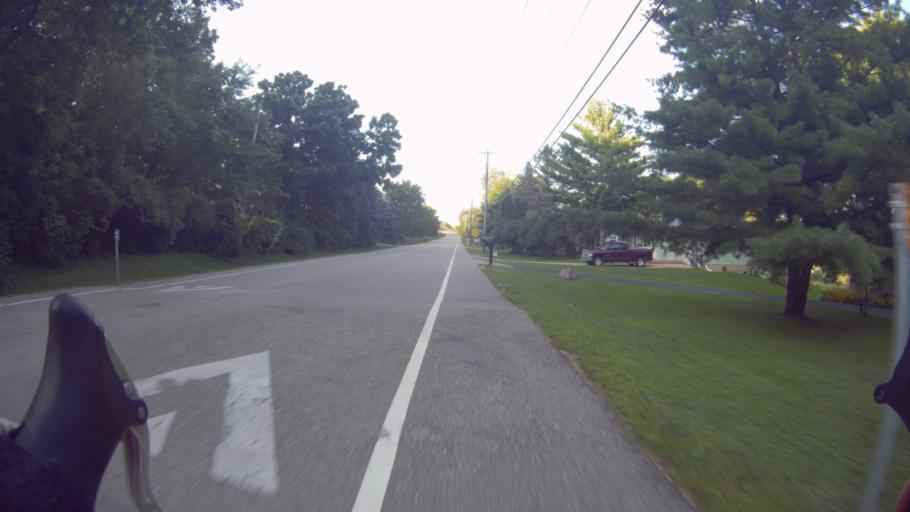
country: US
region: Wisconsin
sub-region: Dane County
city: Madison
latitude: 43.0136
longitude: -89.4243
